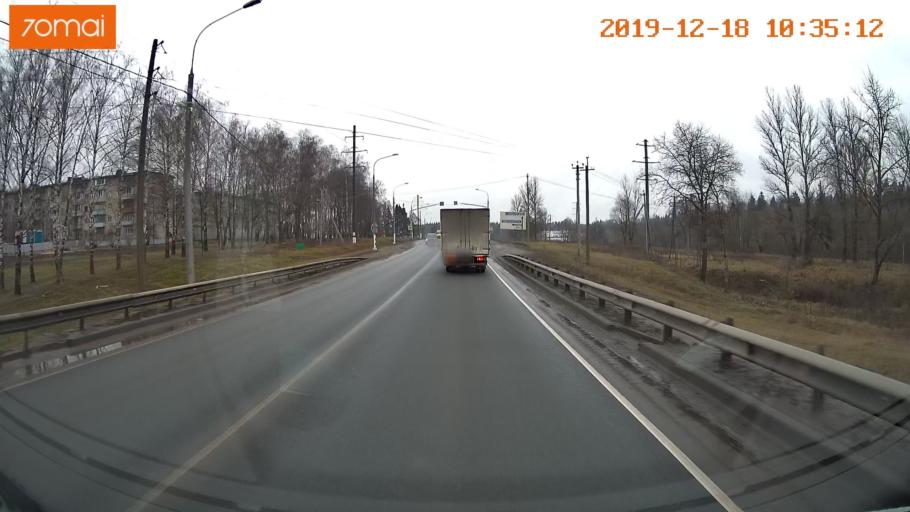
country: RU
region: Moskovskaya
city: Troitsk
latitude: 55.4129
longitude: 37.1959
